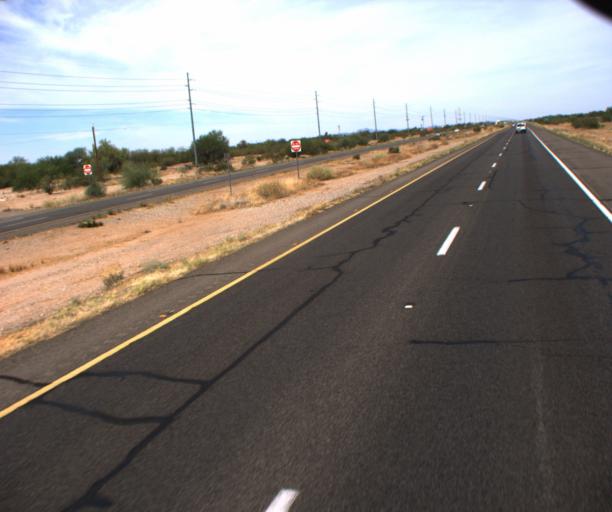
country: US
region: Arizona
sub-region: Maricopa County
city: Sun City West
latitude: 33.7223
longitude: -112.4572
